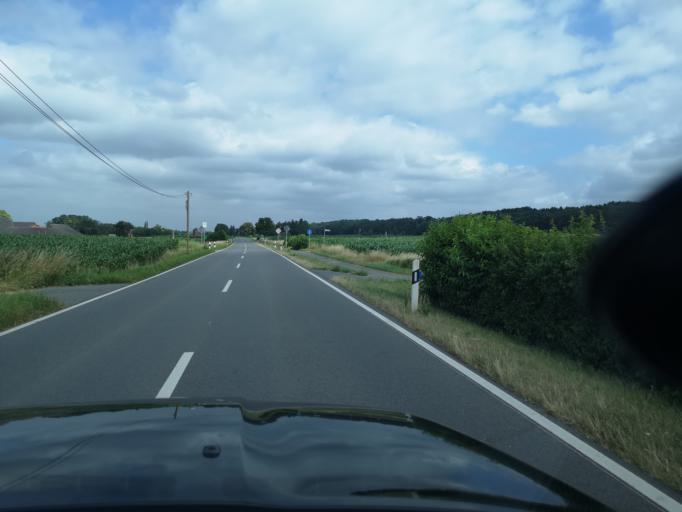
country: DE
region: North Rhine-Westphalia
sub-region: Regierungsbezirk Dusseldorf
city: Hamminkeln
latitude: 51.7346
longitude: 6.6502
